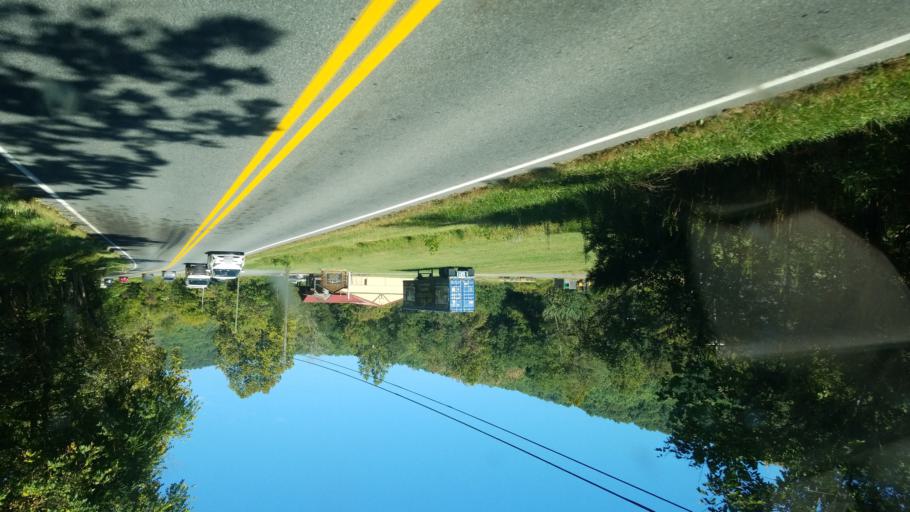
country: US
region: Virginia
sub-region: Greene County
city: Stanardsville
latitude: 38.3370
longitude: -78.5043
